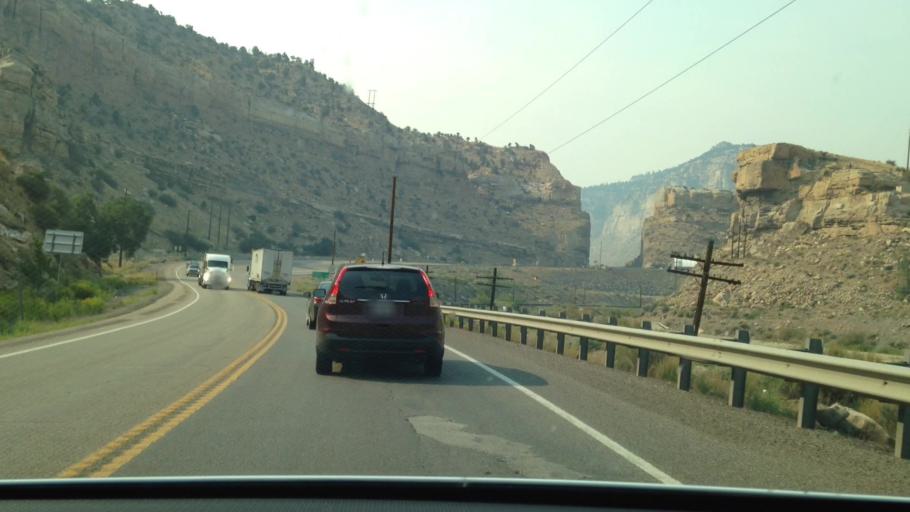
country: US
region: Utah
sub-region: Carbon County
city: Helper
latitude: 39.7234
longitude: -110.8658
